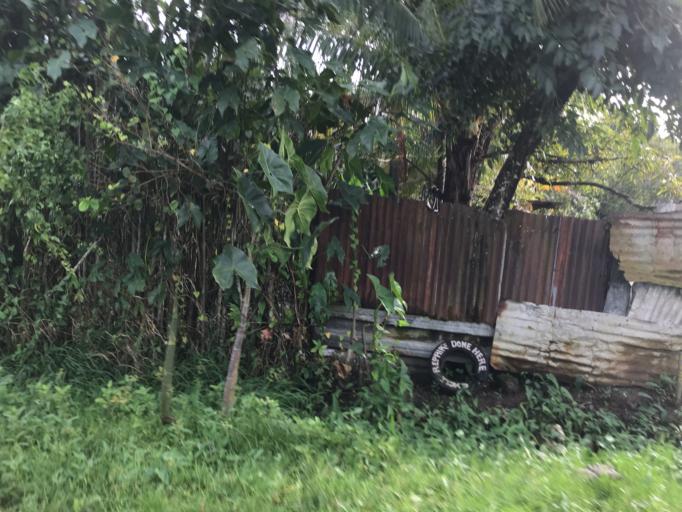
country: GY
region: Demerara-Mahaica
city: Georgetown
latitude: 6.8039
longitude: -58.1280
